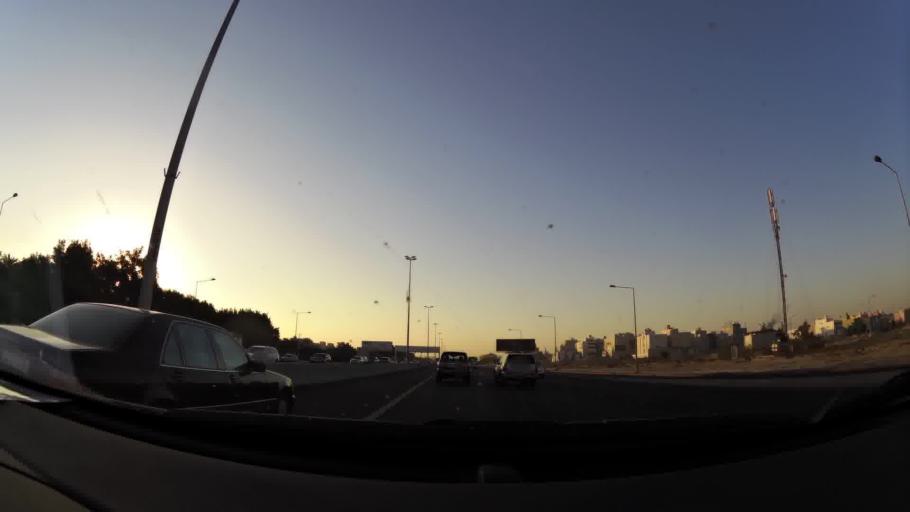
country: KW
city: Al Funaytis
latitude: 29.2078
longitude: 48.1048
